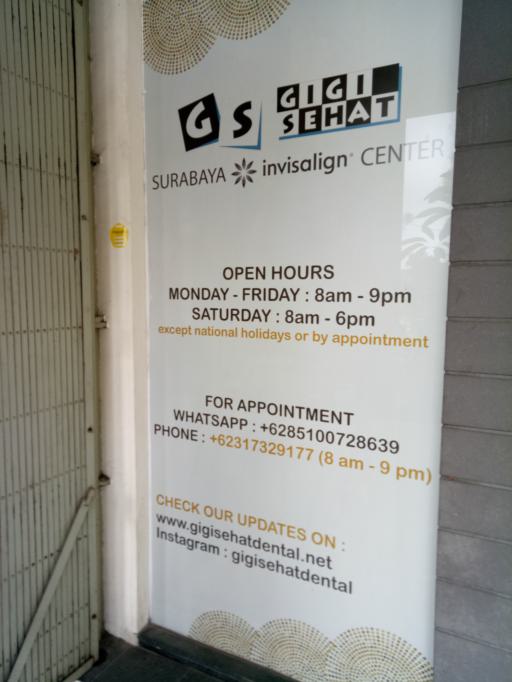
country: ID
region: East Java
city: Jagirsidosermo
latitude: -7.2875
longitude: 112.6791
